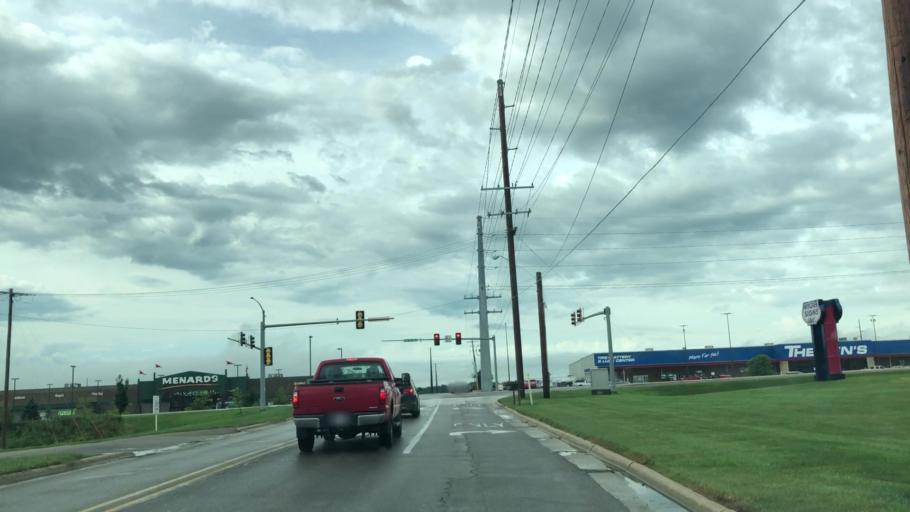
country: US
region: Iowa
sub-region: Marshall County
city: Marshalltown
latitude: 42.0078
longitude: -92.9222
